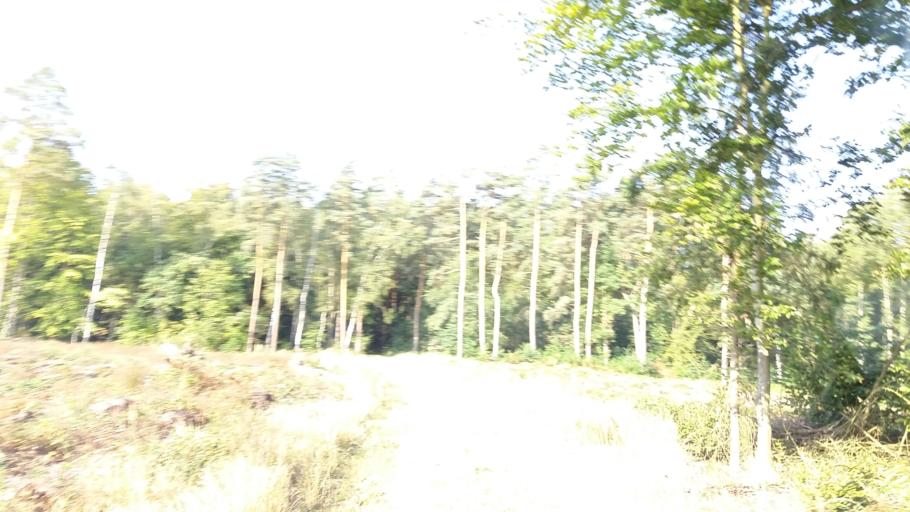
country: PL
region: West Pomeranian Voivodeship
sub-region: Powiat choszczenski
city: Choszczno
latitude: 53.2405
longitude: 15.4218
